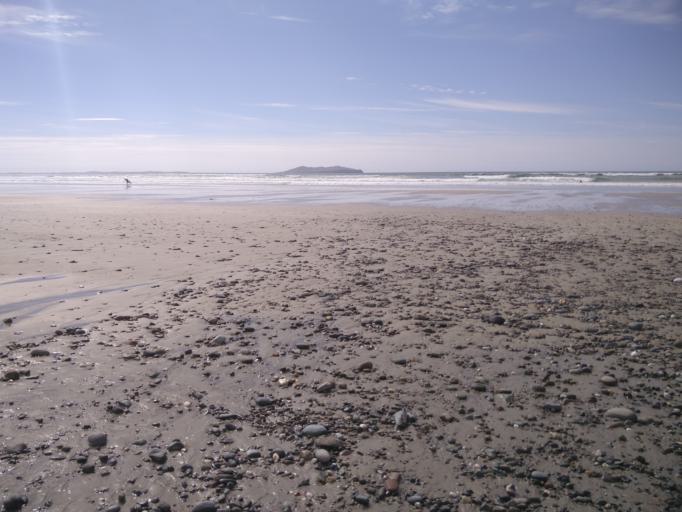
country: IE
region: Connaught
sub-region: County Galway
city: Clifden
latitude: 53.7350
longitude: -9.8943
